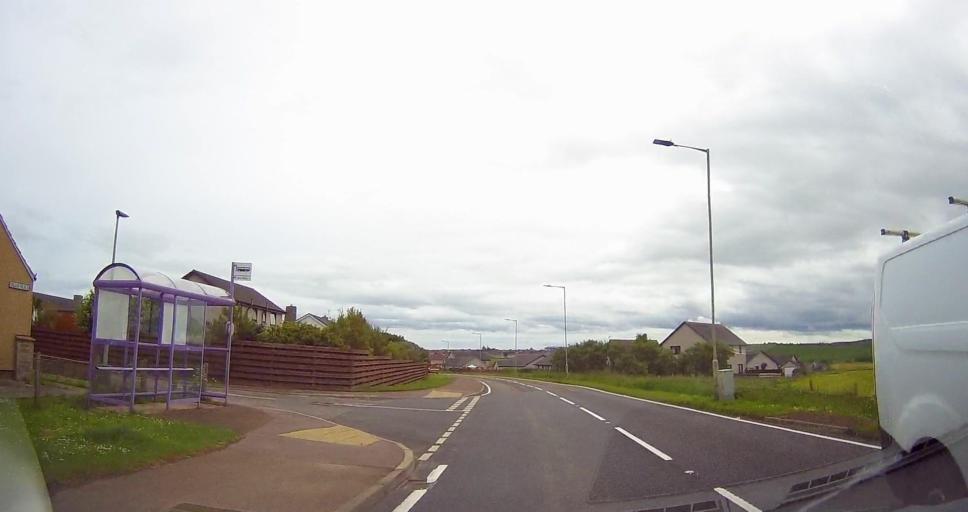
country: GB
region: Scotland
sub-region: Highland
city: Thurso
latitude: 58.6036
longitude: -3.5495
